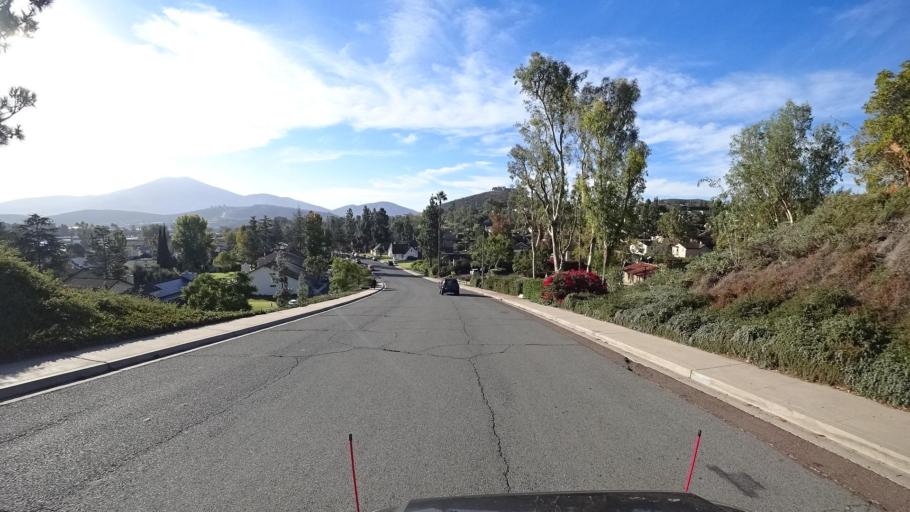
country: US
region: California
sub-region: San Diego County
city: Spring Valley
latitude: 32.7348
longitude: -116.9776
